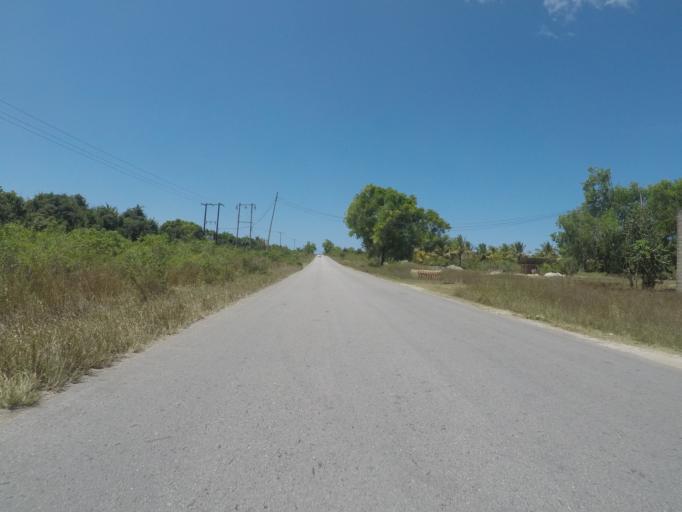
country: TZ
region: Zanzibar Central/South
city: Nganane
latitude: -6.2759
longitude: 39.4862
